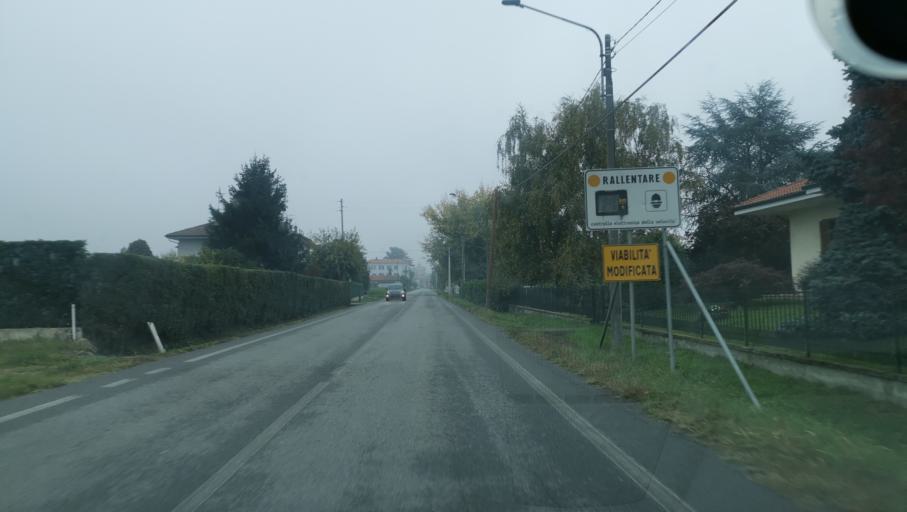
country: IT
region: Piedmont
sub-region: Provincia di Biella
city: Cavaglia
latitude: 45.3978
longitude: 8.0907
